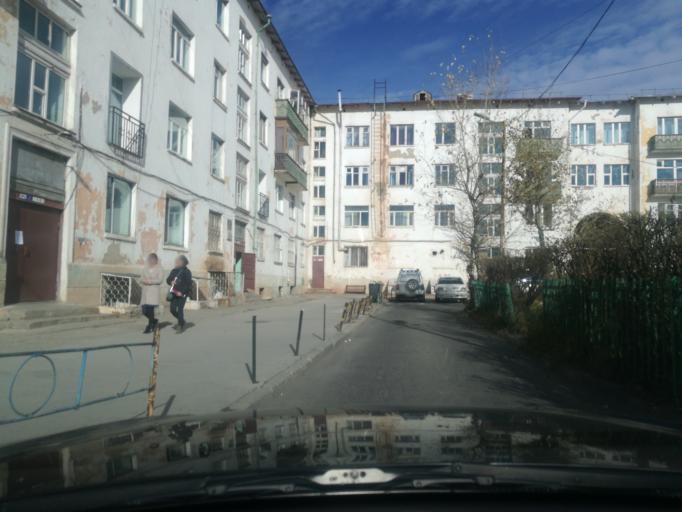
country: MN
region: Ulaanbaatar
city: Ulaanbaatar
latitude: 47.9154
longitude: 106.9074
